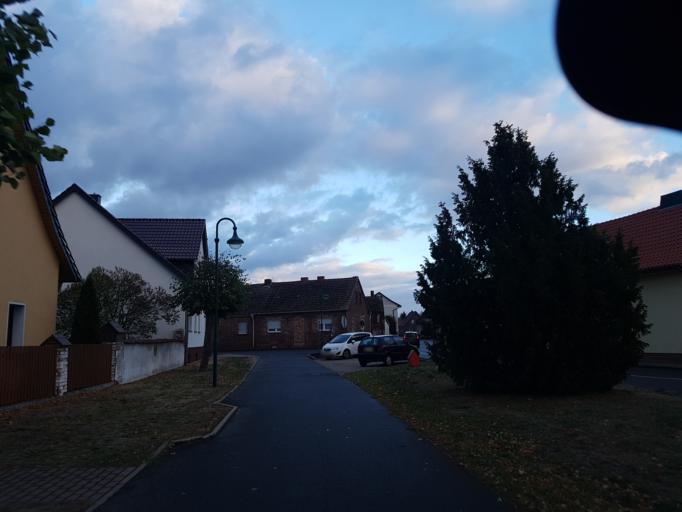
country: DE
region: Saxony-Anhalt
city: Annaburg
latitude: 51.7832
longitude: 13.0656
